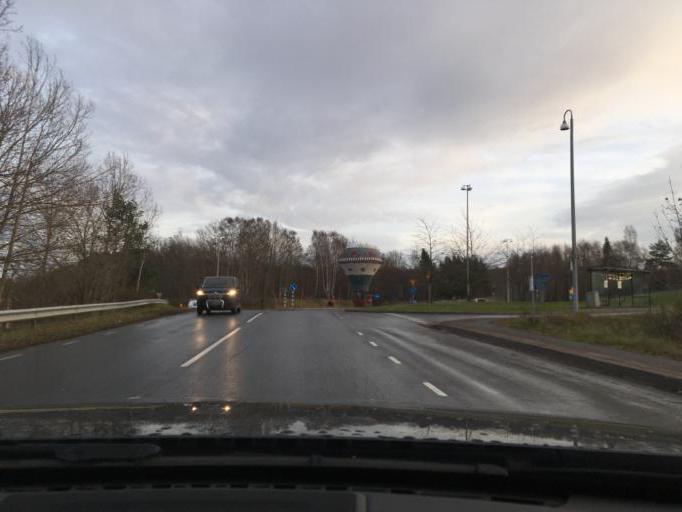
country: SE
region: Joenkoeping
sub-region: Jonkopings Kommun
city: Graenna
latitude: 58.0024
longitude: 14.4512
